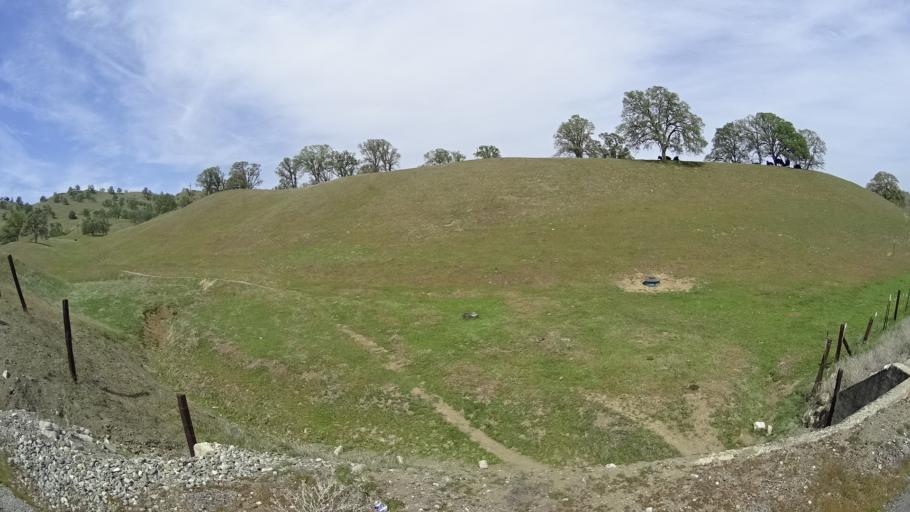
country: US
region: California
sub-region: Glenn County
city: Willows
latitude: 39.6121
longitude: -122.5757
